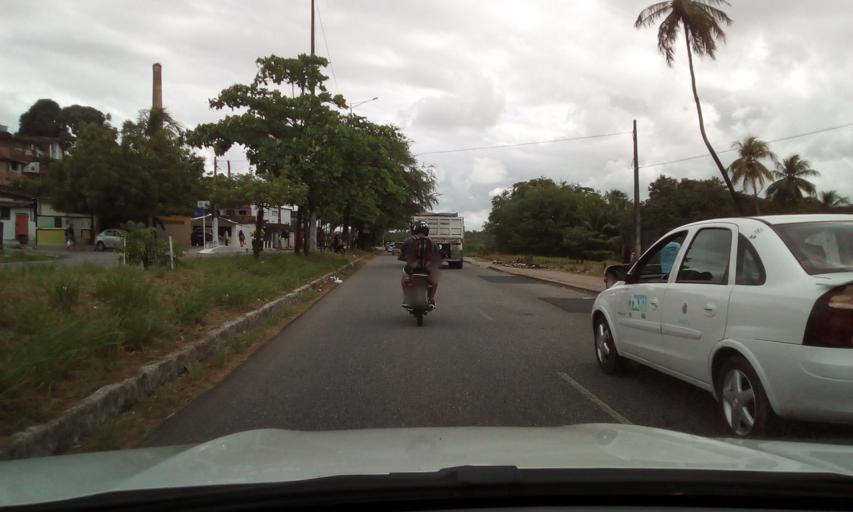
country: BR
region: Paraiba
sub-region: Joao Pessoa
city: Joao Pessoa
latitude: -7.1191
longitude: -34.8925
